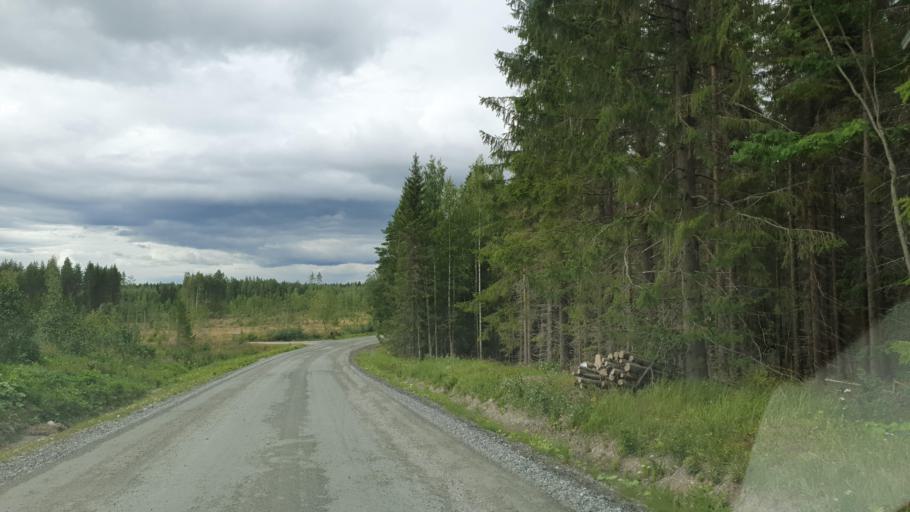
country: FI
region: Northern Savo
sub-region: Ylae-Savo
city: Iisalmi
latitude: 63.5259
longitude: 27.0904
